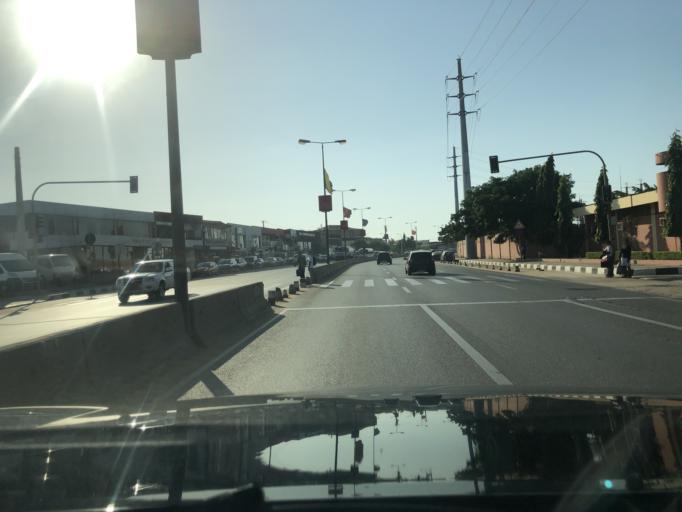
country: AO
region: Luanda
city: Luanda
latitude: -8.9049
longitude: 13.1776
